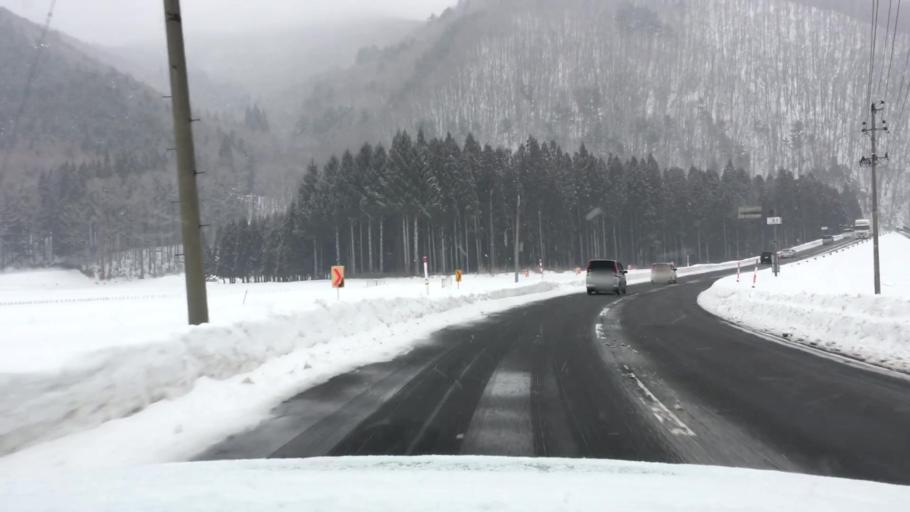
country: JP
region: Akita
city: Hanawa
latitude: 40.0803
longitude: 141.0234
